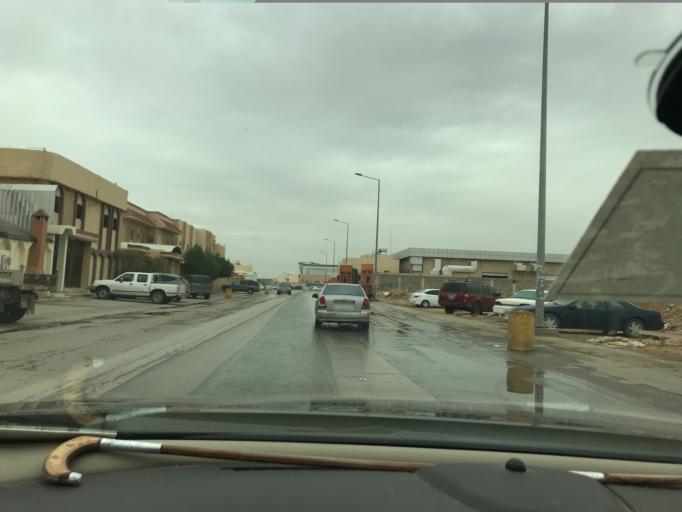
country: SA
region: Ar Riyad
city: Riyadh
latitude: 24.7534
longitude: 46.8282
